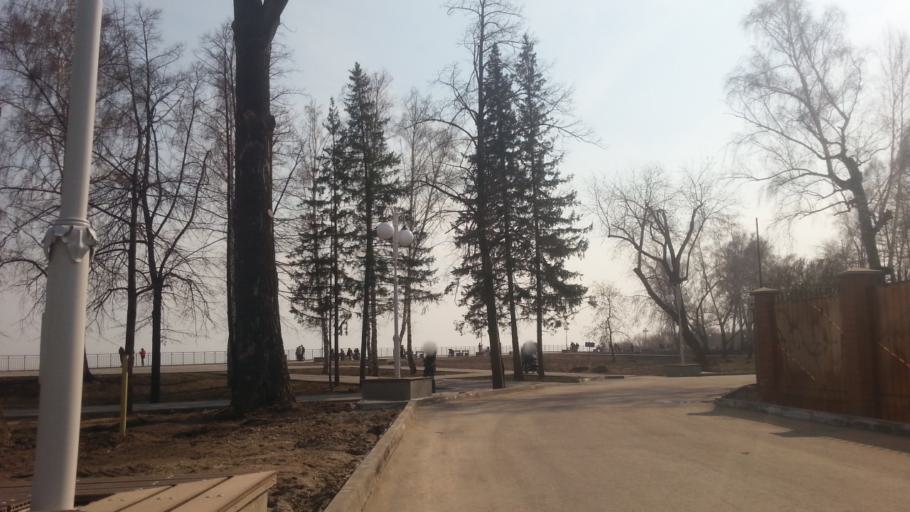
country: RU
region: Altai Krai
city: Zaton
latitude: 53.3228
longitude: 83.7951
